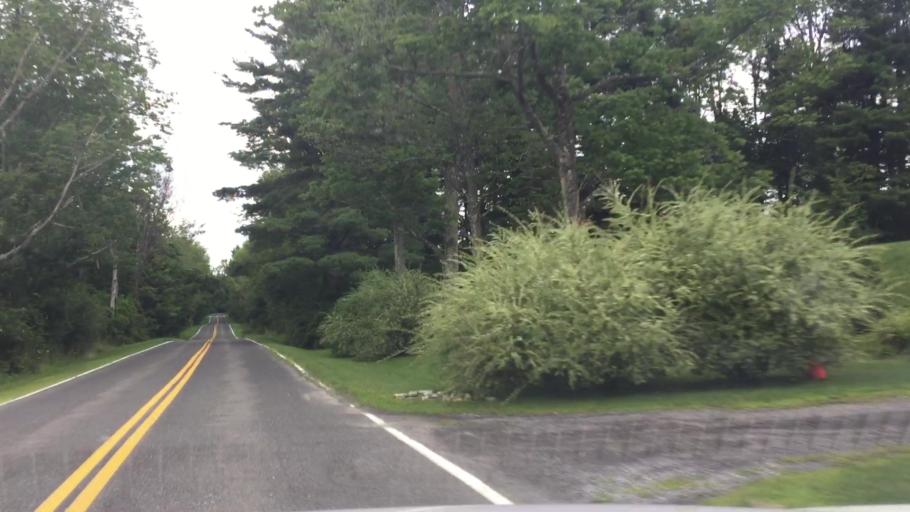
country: US
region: Massachusetts
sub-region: Berkshire County
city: Housatonic
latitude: 42.2769
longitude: -73.4087
